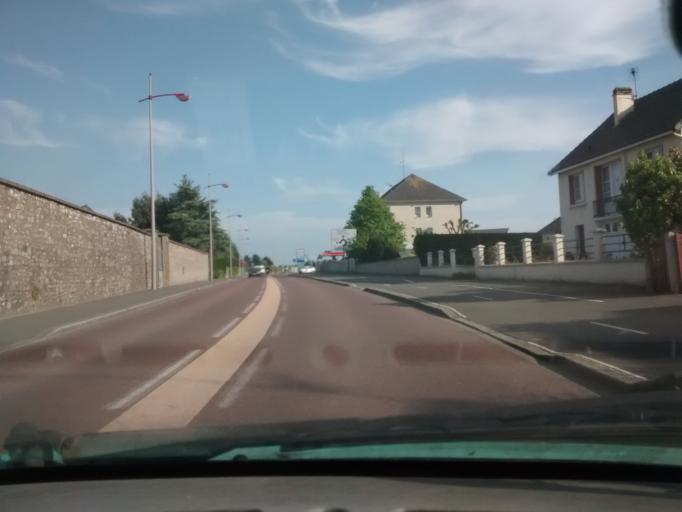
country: FR
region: Lower Normandy
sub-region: Departement de la Manche
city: Lessay
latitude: 49.2149
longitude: -1.5307
